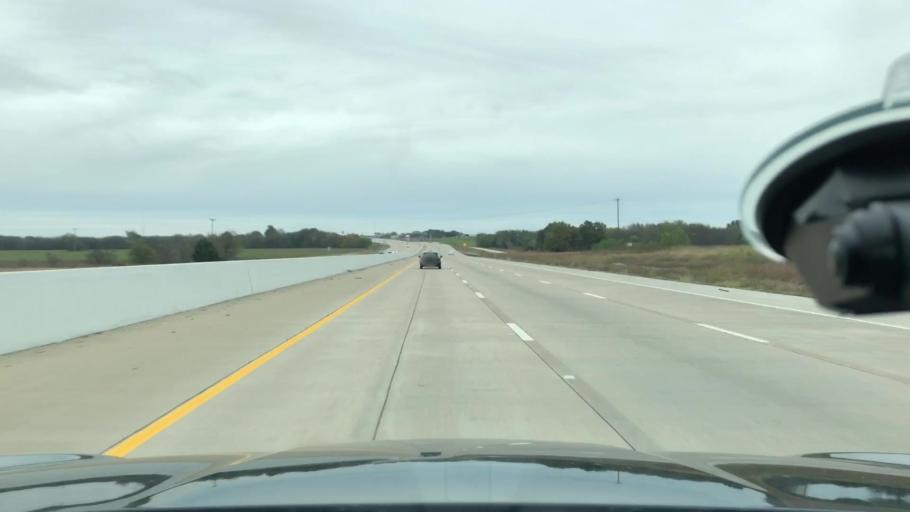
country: US
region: Texas
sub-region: Ellis County
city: Italy
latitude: 32.1681
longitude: -96.9159
